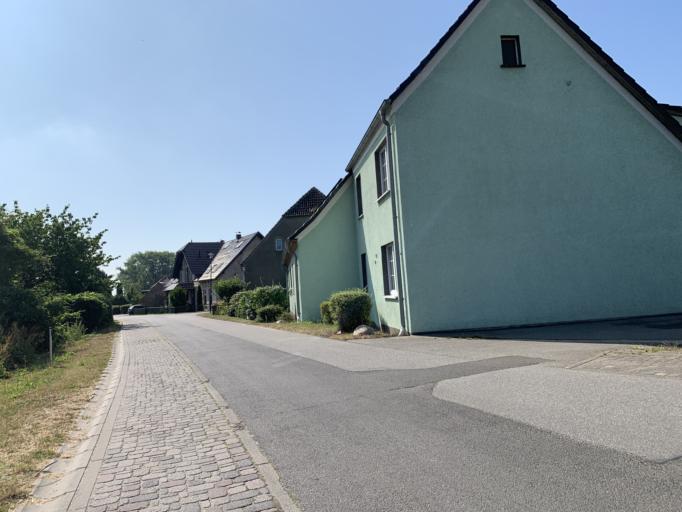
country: PL
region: West Pomeranian Voivodeship
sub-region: Powiat policki
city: Nowe Warpno
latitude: 53.7400
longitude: 14.2677
